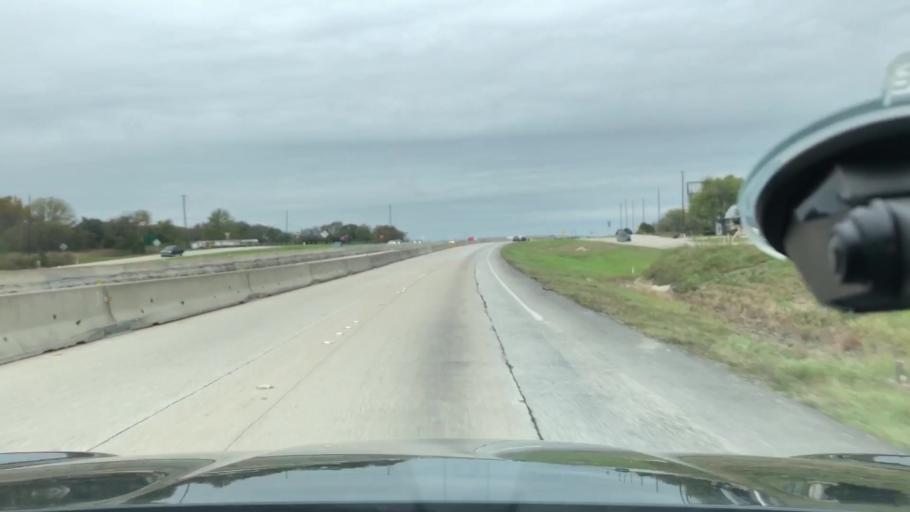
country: US
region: Texas
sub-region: Ellis County
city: Waxahachie
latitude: 32.3746
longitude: -96.8636
